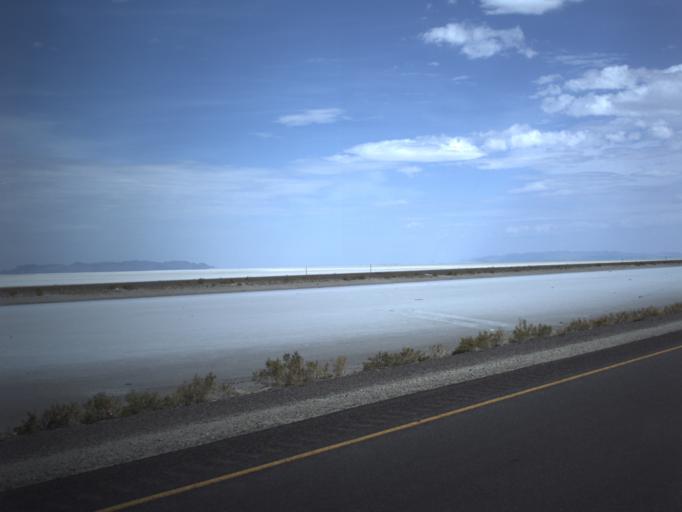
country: US
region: Utah
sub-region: Tooele County
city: Wendover
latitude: 40.7357
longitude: -113.7162
